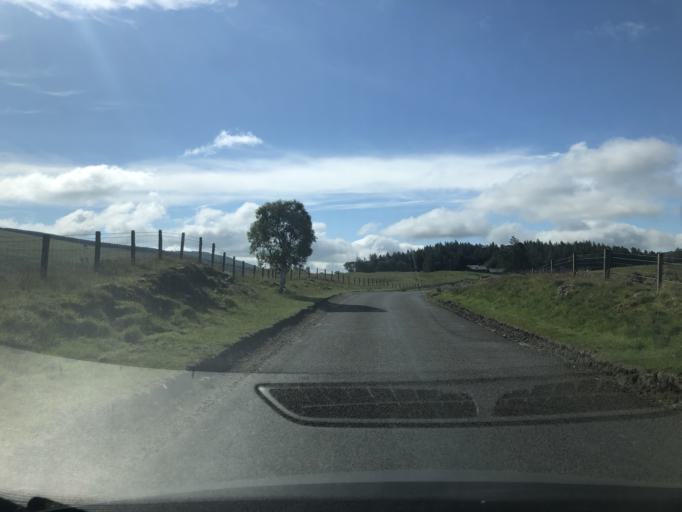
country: GB
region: Scotland
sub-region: Angus
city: Kirriemuir
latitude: 56.7715
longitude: -3.0263
